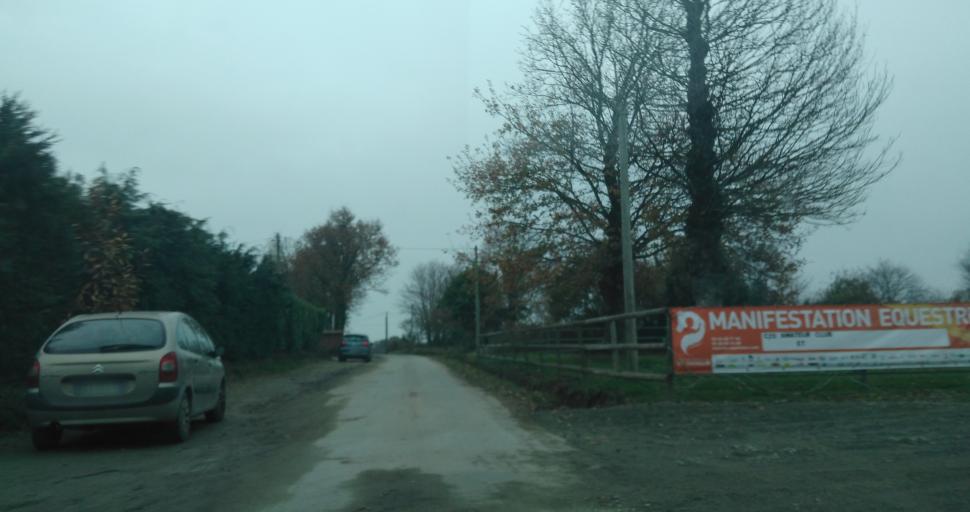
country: FR
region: Brittany
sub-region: Departement d'Ille-et-Vilaine
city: Iffendic
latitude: 48.1055
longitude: -2.0338
